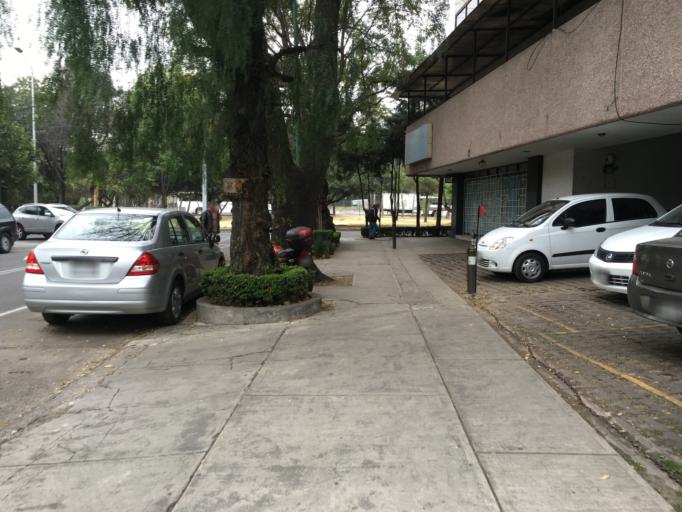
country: MX
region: Mexico
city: Colonia Lindavista
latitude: 19.4897
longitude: -99.1231
